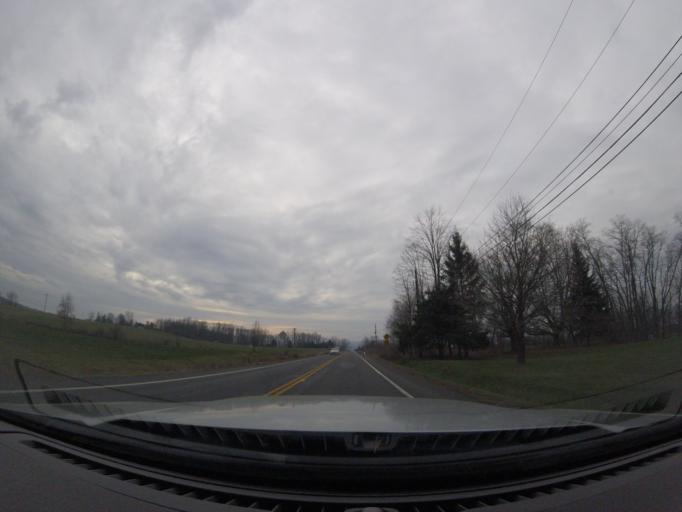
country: US
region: New York
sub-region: Schuyler County
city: Watkins Glen
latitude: 42.4091
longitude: -76.8528
